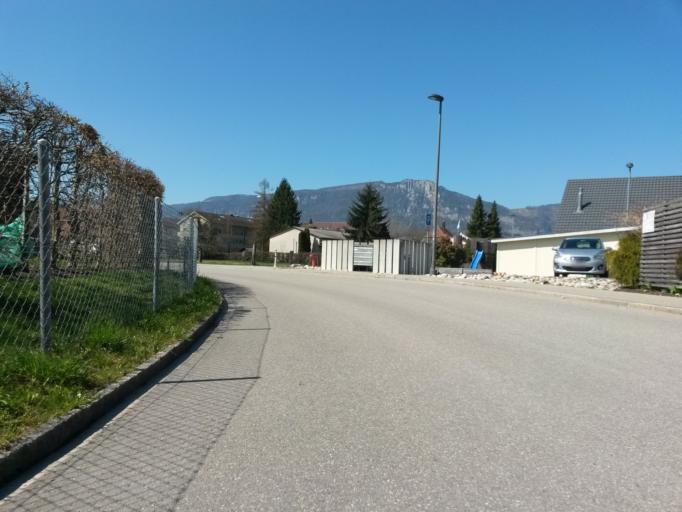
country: CH
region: Solothurn
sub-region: Bezirk Wasseramt
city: Luterbach
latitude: 47.2155
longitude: 7.5913
